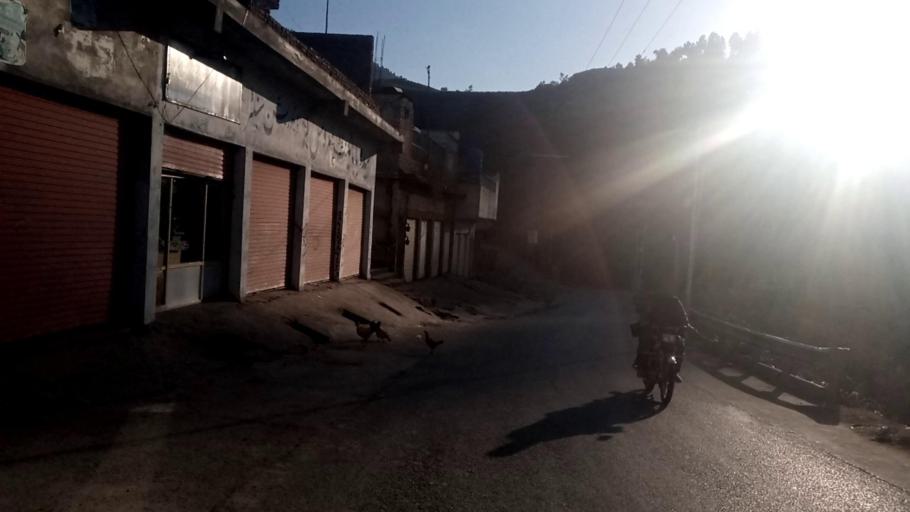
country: PK
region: Khyber Pakhtunkhwa
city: Saidu Sharif
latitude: 34.7434
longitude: 72.3520
